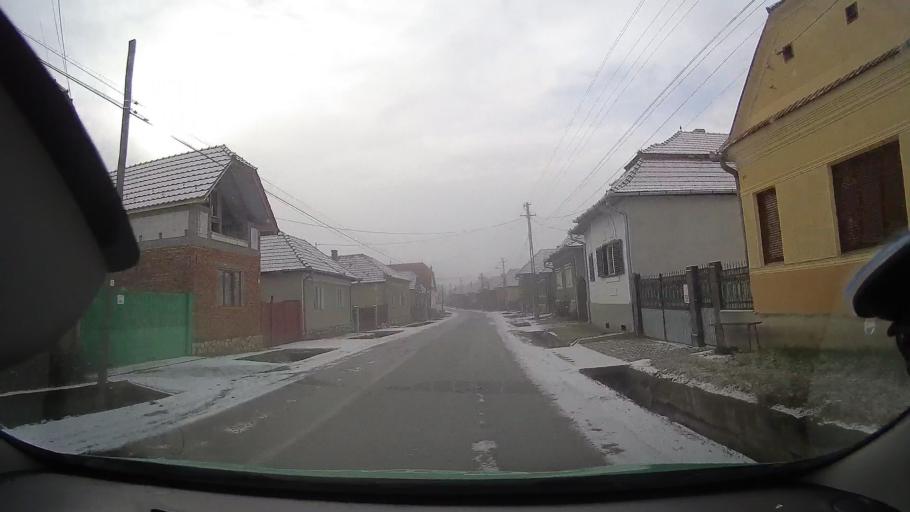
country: RO
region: Alba
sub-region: Comuna Rimetea
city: Rimetea
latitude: 46.4210
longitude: 23.5608
